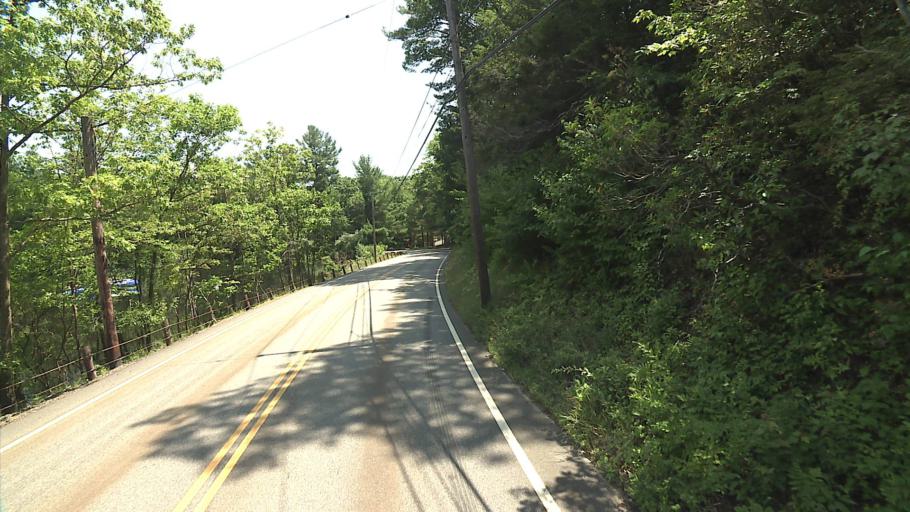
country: US
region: Connecticut
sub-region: Litchfield County
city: Winchester Center
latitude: 41.9158
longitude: -73.1099
